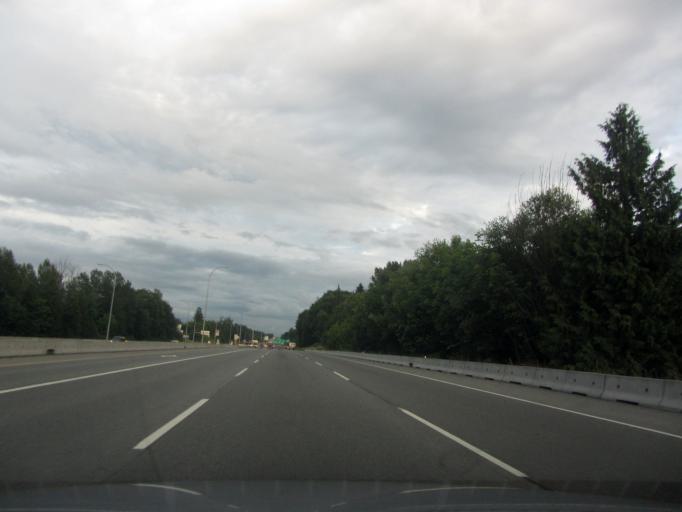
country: CA
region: British Columbia
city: Pitt Meadows
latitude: 49.1734
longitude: -122.7047
